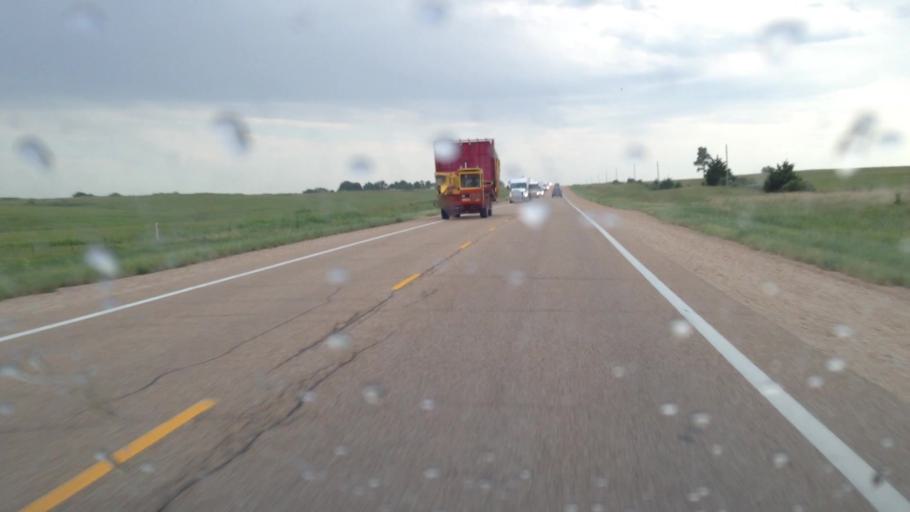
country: US
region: Kansas
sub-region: Coffey County
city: Burlington
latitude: 38.1491
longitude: -95.7392
